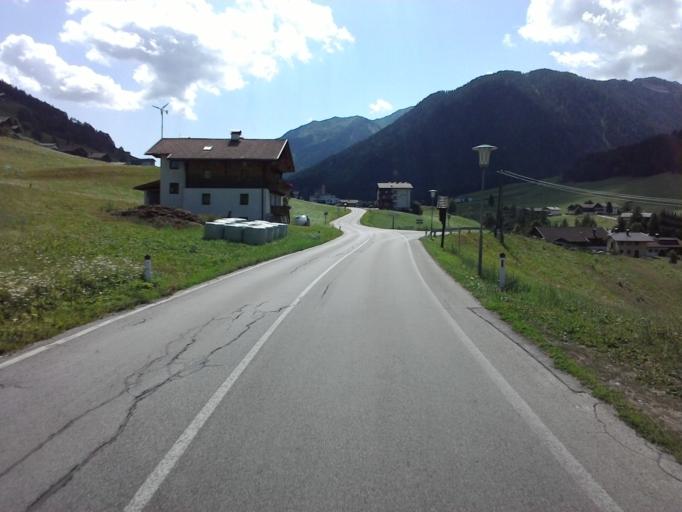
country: AT
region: Tyrol
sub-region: Politischer Bezirk Lienz
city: Kartitsch
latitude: 46.7304
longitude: 12.4893
